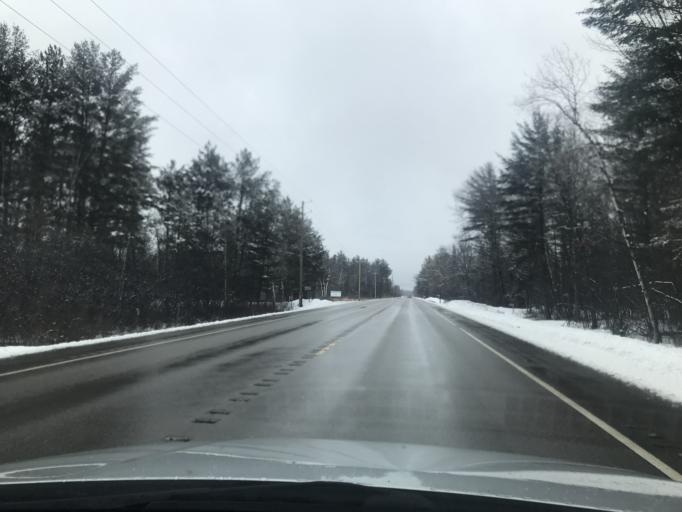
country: US
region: Wisconsin
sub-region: Marinette County
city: Marinette
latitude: 45.1341
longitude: -87.6888
